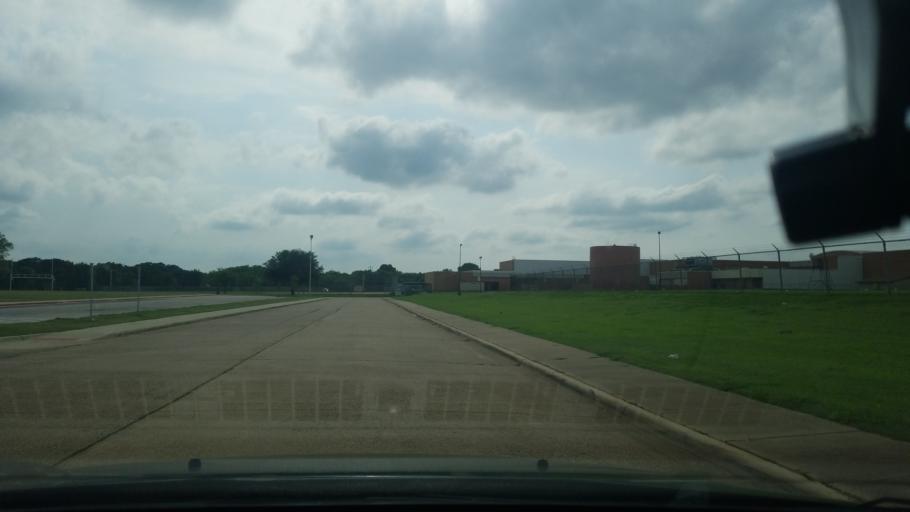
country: US
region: Texas
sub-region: Dallas County
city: Balch Springs
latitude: 32.7599
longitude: -96.6336
